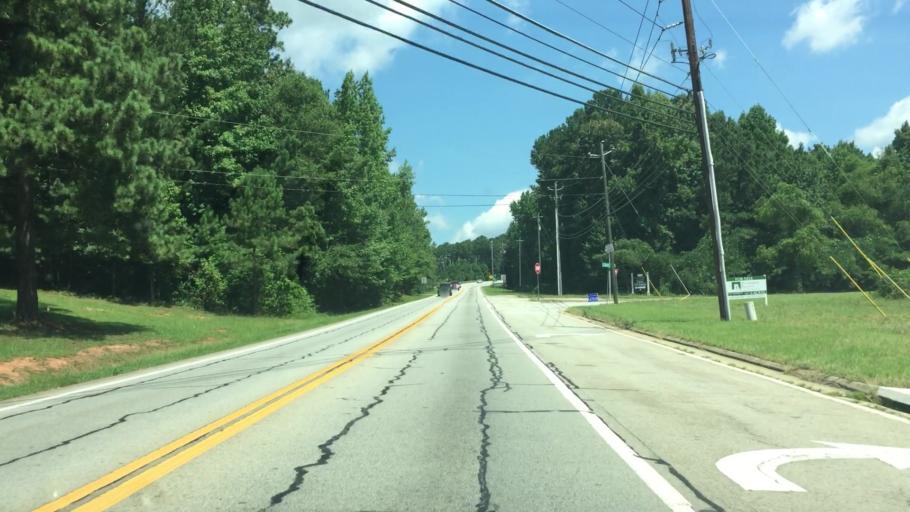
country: US
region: Georgia
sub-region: Henry County
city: Stockbridge
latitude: 33.5362
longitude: -84.2004
